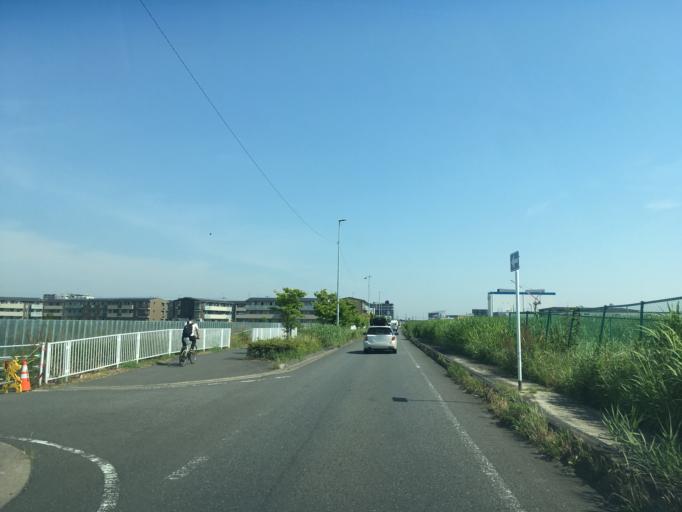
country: JP
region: Saitama
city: Yoshikawa
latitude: 35.8693
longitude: 139.8279
